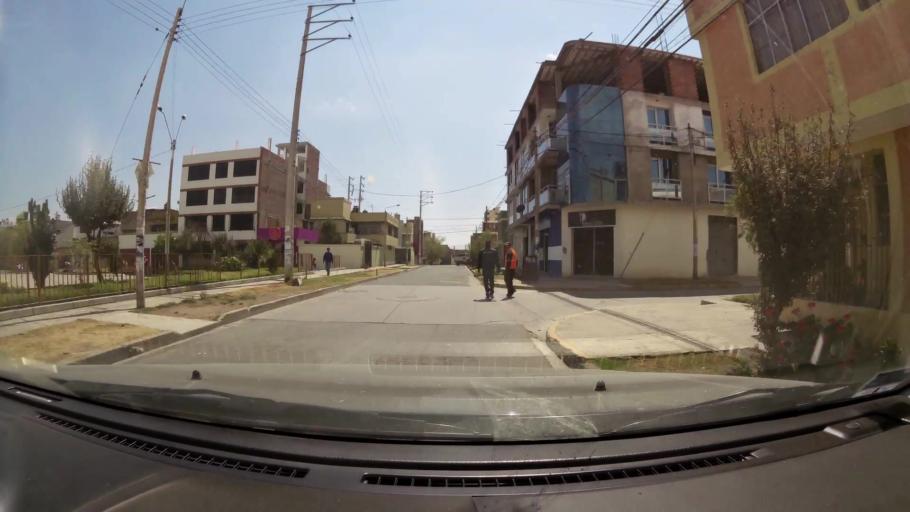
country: PE
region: Junin
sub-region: Provincia de Huancayo
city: El Tambo
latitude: -12.0664
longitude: -75.2184
